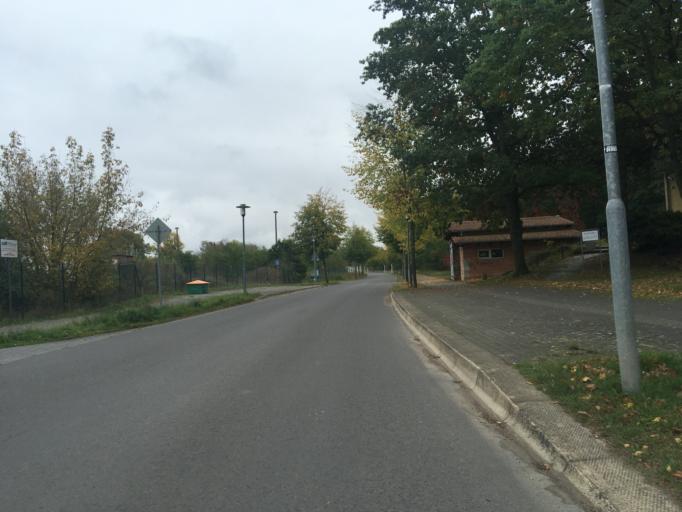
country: DE
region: Brandenburg
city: Brieselang
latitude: 52.5456
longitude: 12.9988
